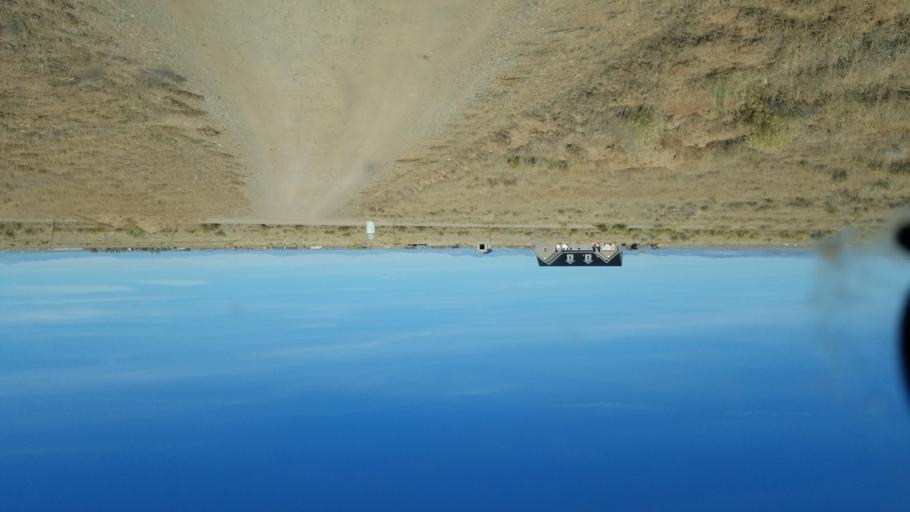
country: US
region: Colorado
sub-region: Rio Grande County
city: Monte Vista
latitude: 37.4007
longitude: -106.1201
